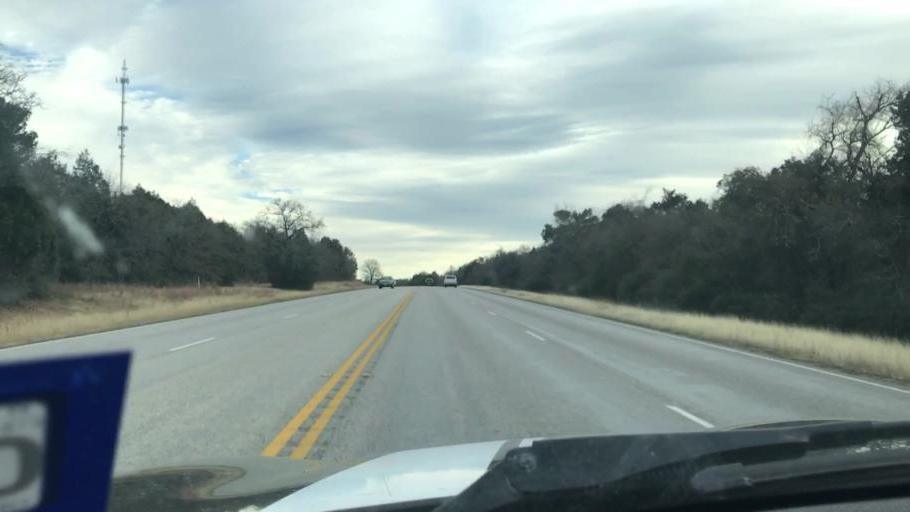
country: US
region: Texas
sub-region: Bastrop County
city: Camp Swift
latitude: 30.2520
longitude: -97.2252
